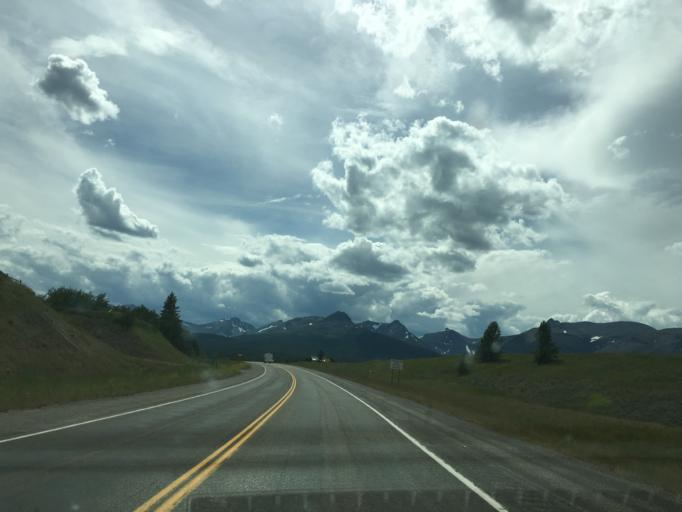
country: US
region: Montana
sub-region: Glacier County
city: South Browning
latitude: 48.4495
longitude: -113.2092
